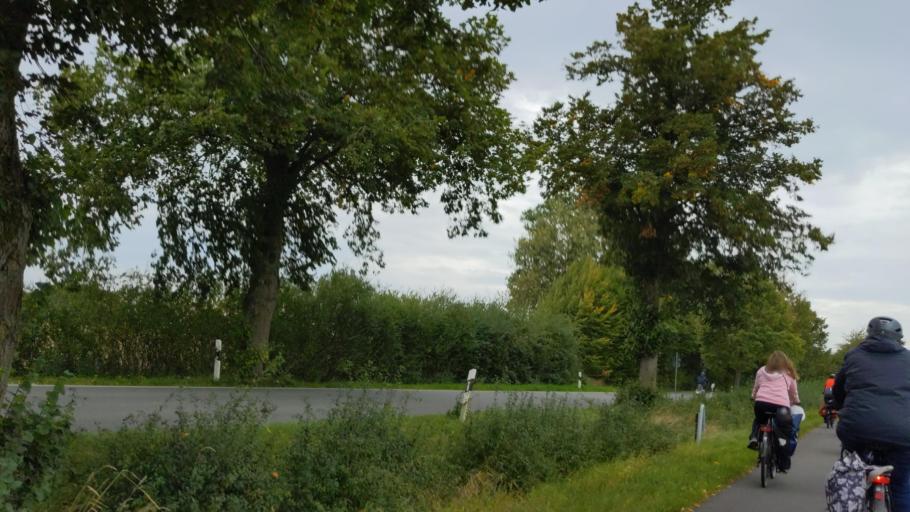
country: DE
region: Mecklenburg-Vorpommern
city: Schlagsdorf
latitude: 53.7612
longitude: 10.7902
